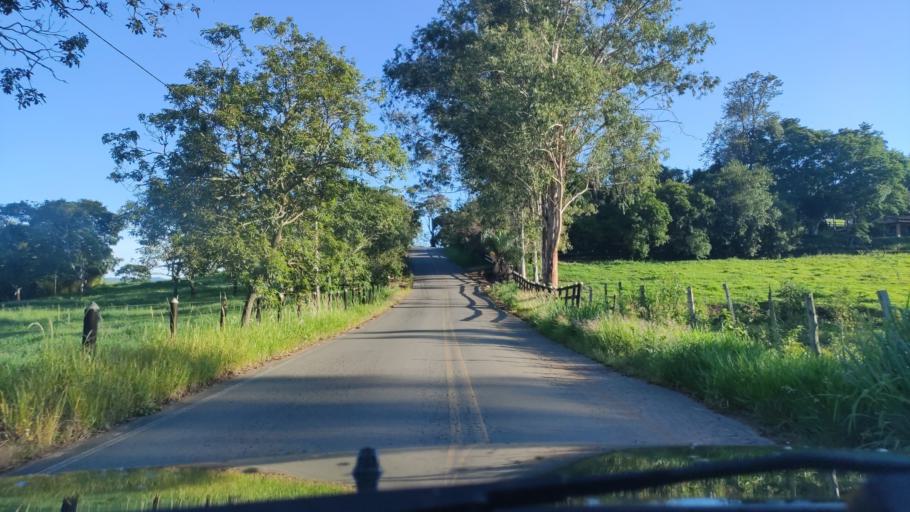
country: BR
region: Sao Paulo
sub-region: Serra Negra
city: Serra Negra
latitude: -22.5909
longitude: -46.6257
